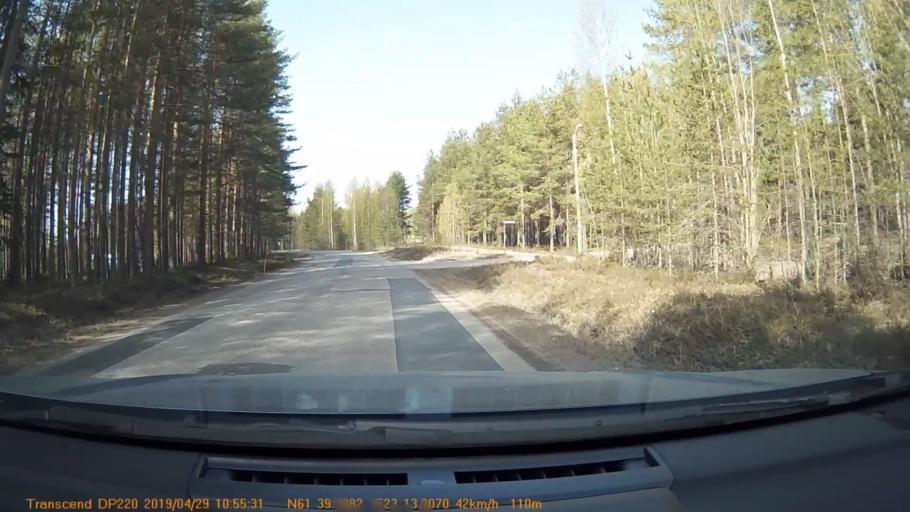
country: FI
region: Pirkanmaa
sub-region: Tampere
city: Haemeenkyroe
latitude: 61.6631
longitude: 23.2303
